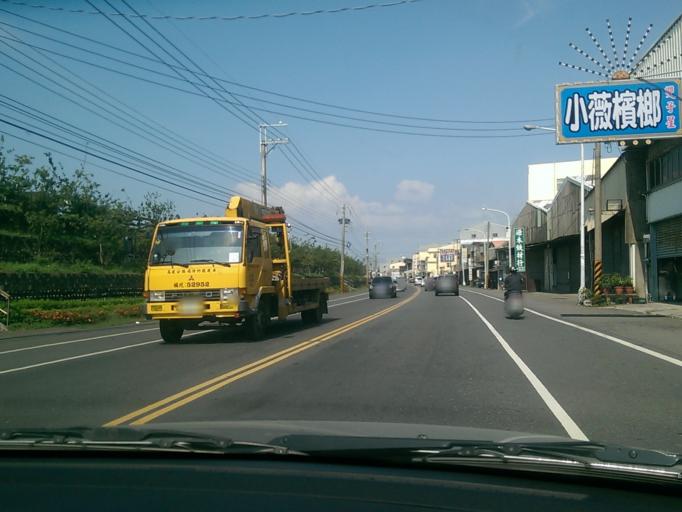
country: TW
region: Taiwan
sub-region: Chiayi
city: Taibao
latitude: 23.5600
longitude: 120.3064
